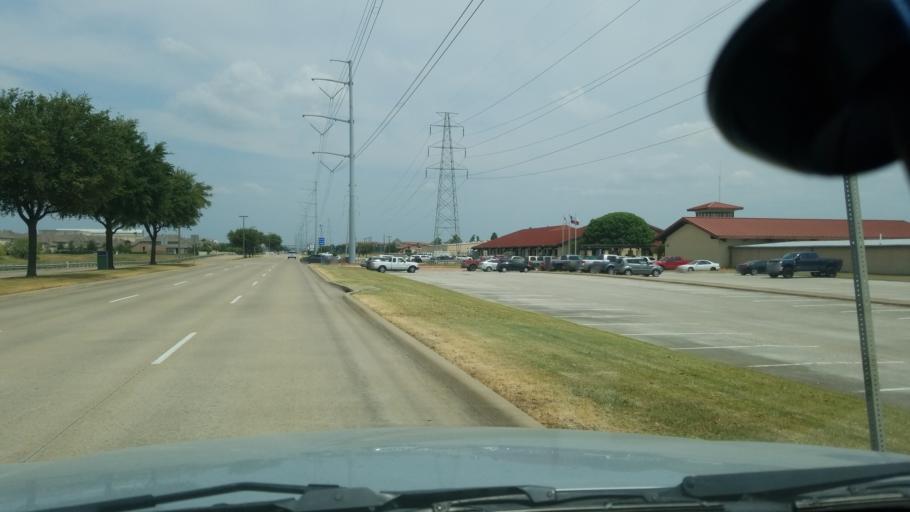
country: US
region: Texas
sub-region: Dallas County
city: Farmers Branch
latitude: 32.8881
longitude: -96.9348
